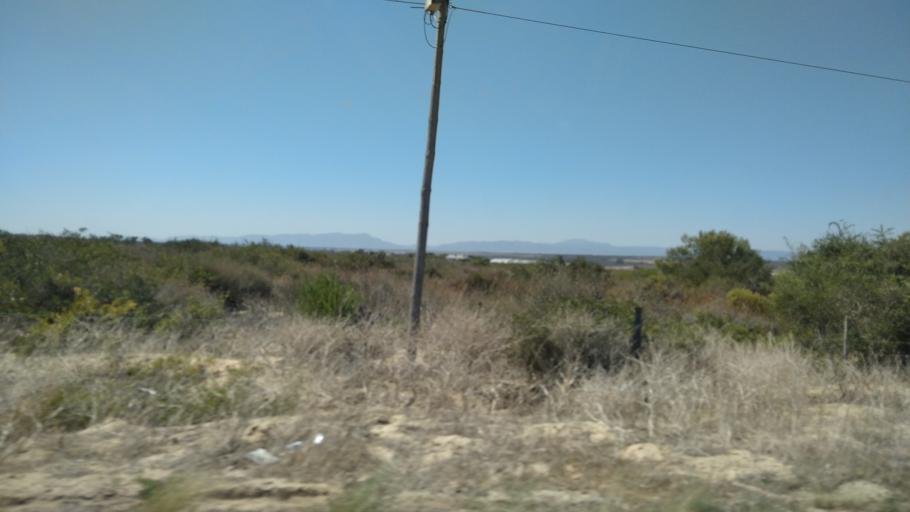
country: ZA
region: Western Cape
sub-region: West Coast District Municipality
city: Moorreesburg
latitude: -33.0513
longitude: 18.3333
